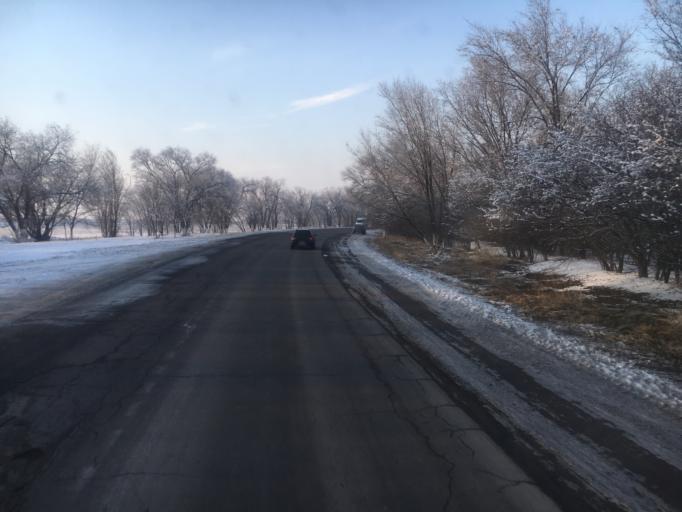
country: KZ
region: Almaty Oblysy
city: Burunday
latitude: 43.3076
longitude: 76.6674
